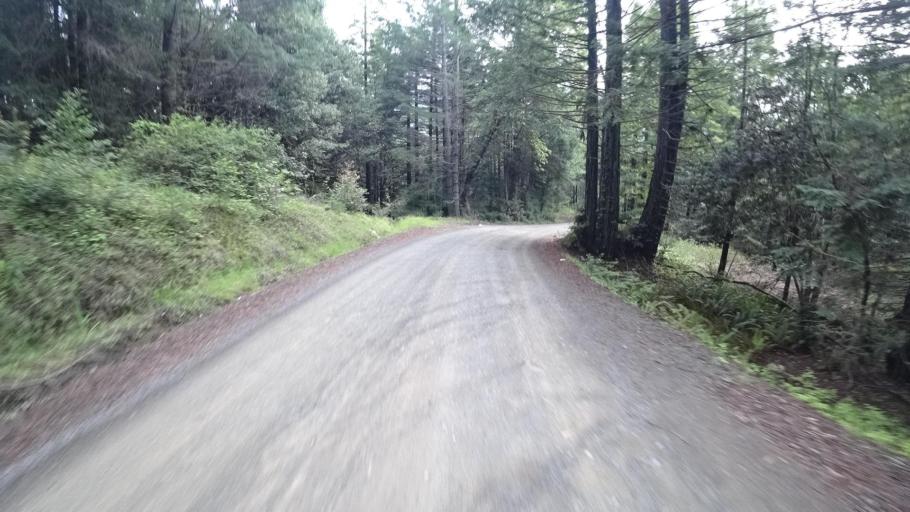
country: US
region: California
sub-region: Humboldt County
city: Redway
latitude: 40.3181
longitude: -123.8299
